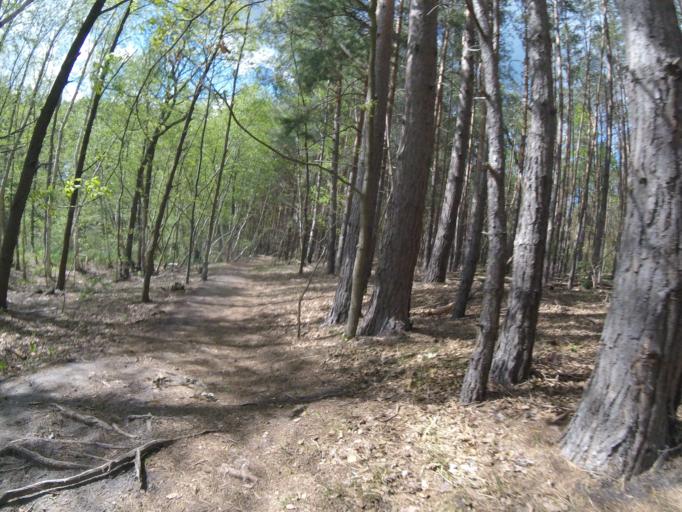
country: DE
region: Brandenburg
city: Teupitz
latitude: 52.1169
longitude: 13.6147
